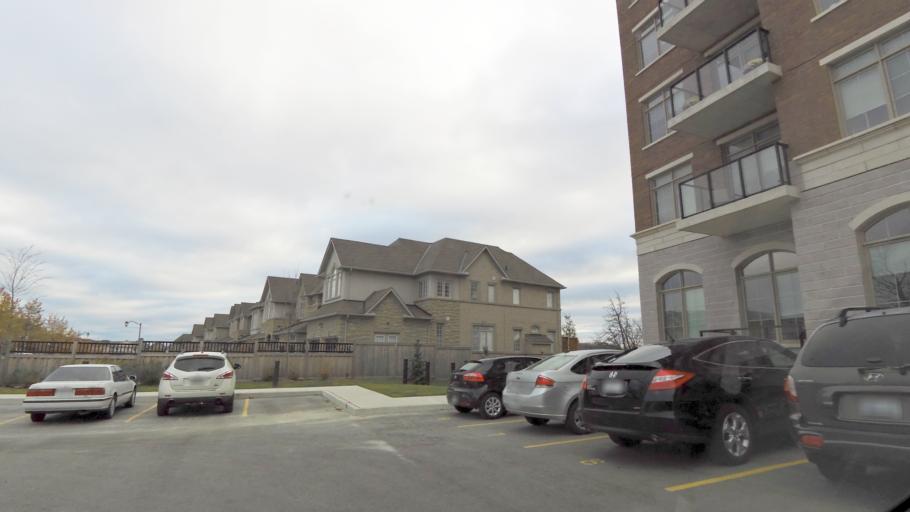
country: CA
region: Ontario
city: Burlington
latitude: 43.4316
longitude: -79.7794
